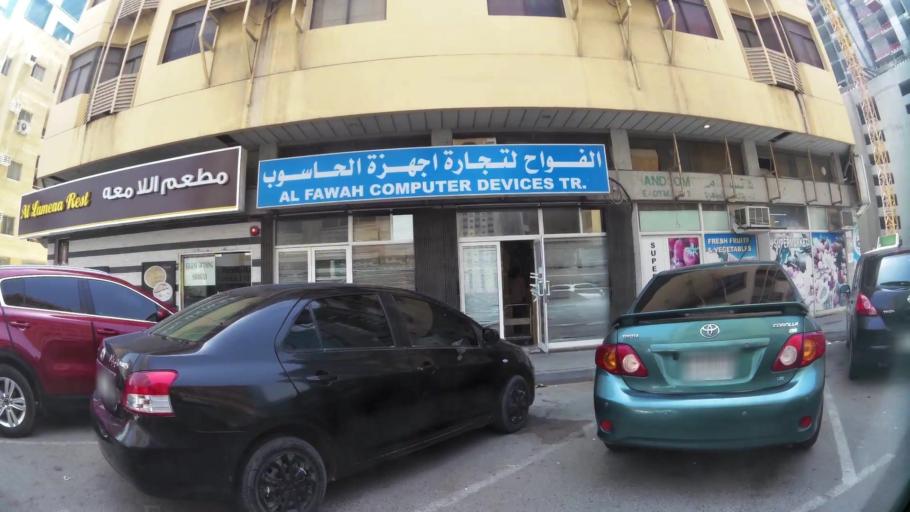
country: AE
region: Ash Shariqah
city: Sharjah
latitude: 25.3430
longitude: 55.3865
